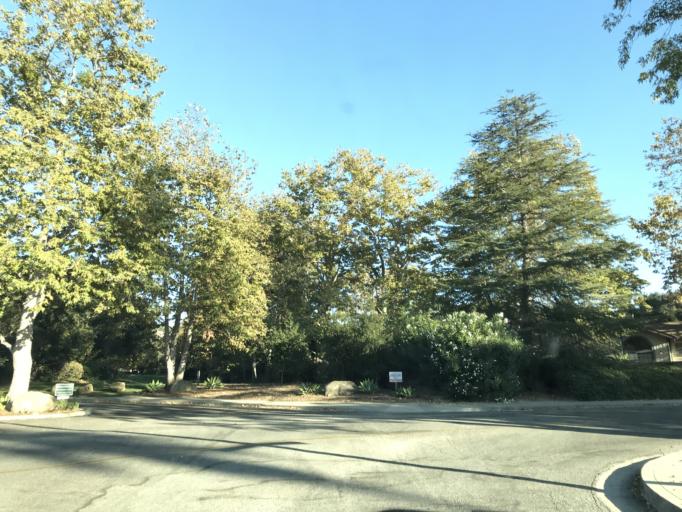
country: US
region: California
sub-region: Santa Barbara County
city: Goleta
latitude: 34.4509
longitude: -119.8111
